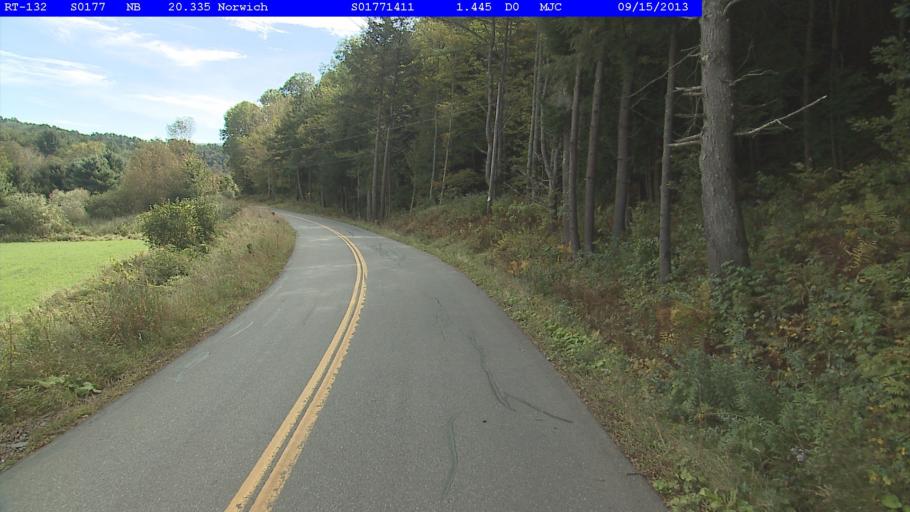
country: US
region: New Hampshire
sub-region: Grafton County
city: Hanover
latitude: 43.7688
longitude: -72.2494
